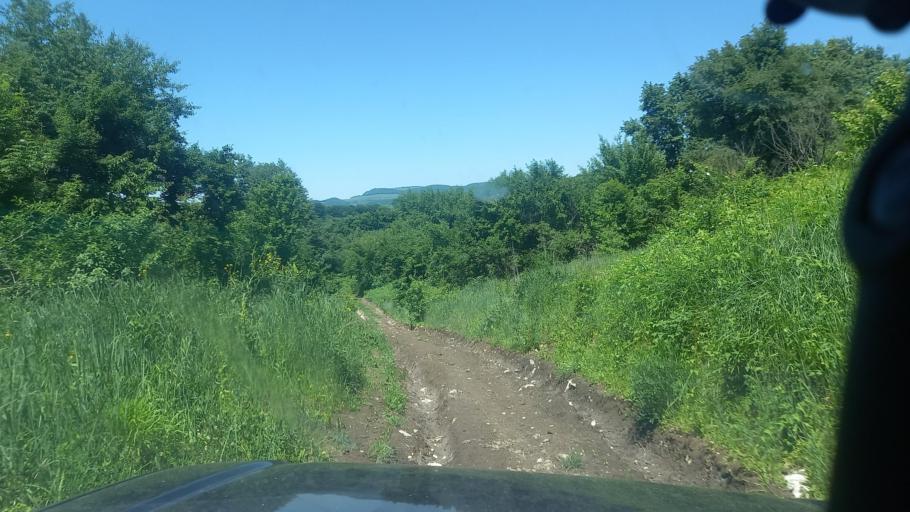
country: RU
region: Karachayevo-Cherkesiya
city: Pregradnaya
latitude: 44.1073
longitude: 41.1288
